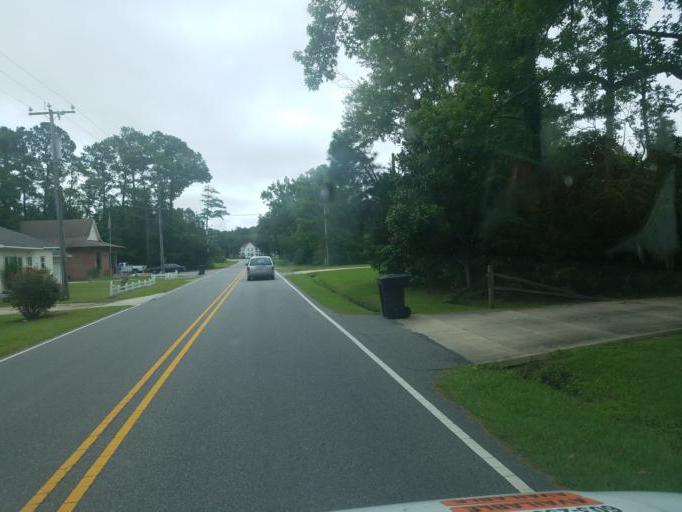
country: US
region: North Carolina
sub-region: Dare County
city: Wanchese
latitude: 35.8466
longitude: -75.6382
